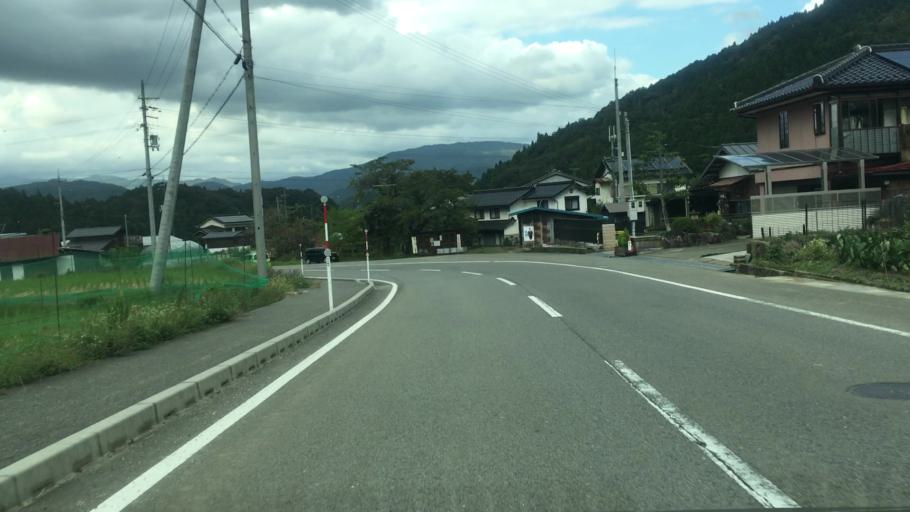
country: JP
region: Hyogo
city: Toyooka
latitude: 35.4387
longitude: 134.7332
